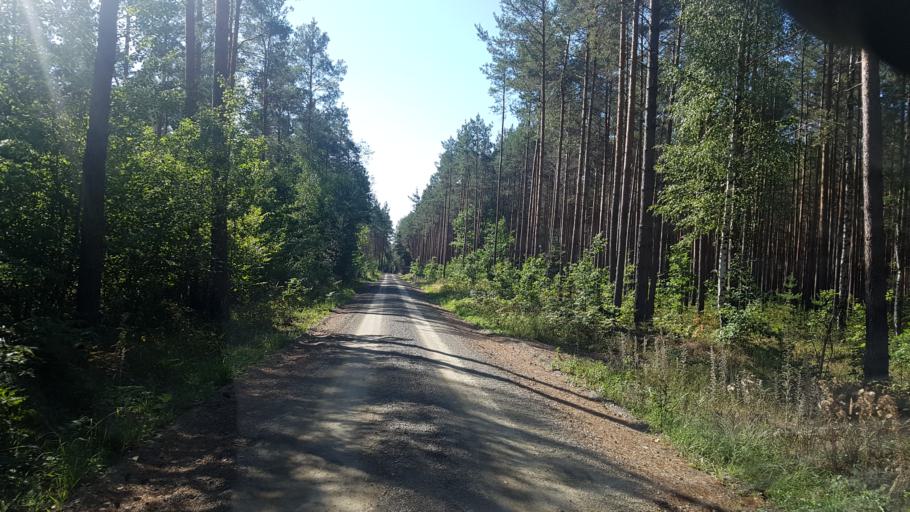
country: DE
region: Brandenburg
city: Ruckersdorf
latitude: 51.5386
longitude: 13.5818
